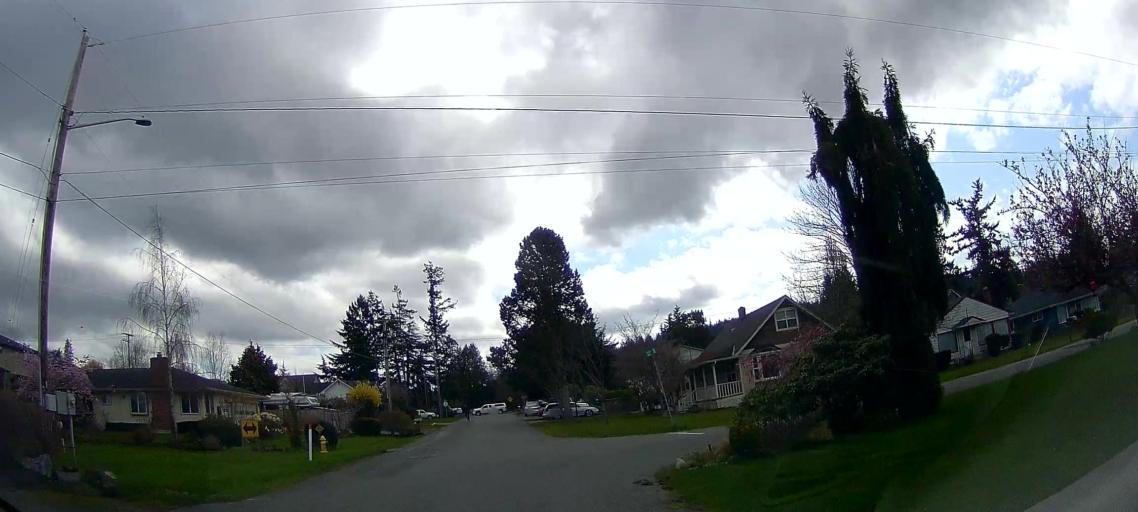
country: US
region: Washington
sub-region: Skagit County
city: Anacortes
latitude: 48.5141
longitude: -122.6329
